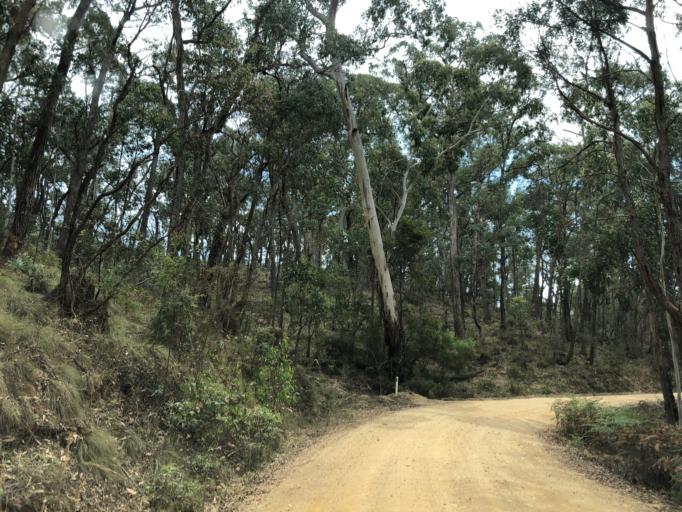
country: AU
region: Victoria
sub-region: Moorabool
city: Bacchus Marsh
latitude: -37.4974
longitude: 144.3536
